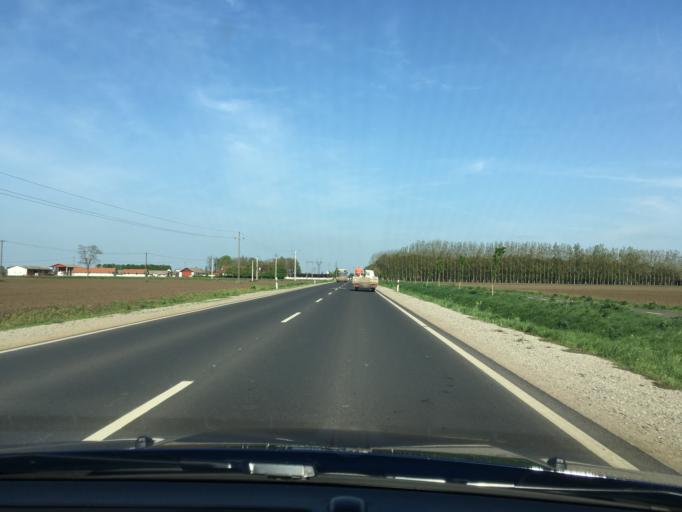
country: HU
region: Bekes
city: Bekescsaba
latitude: 46.6780
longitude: 21.0243
